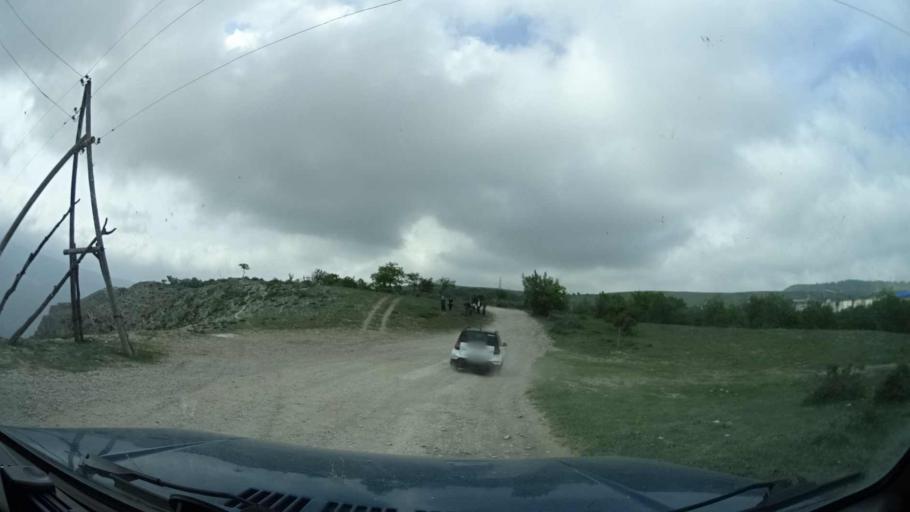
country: RU
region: Dagestan
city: Dubki
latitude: 43.0189
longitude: 46.8323
